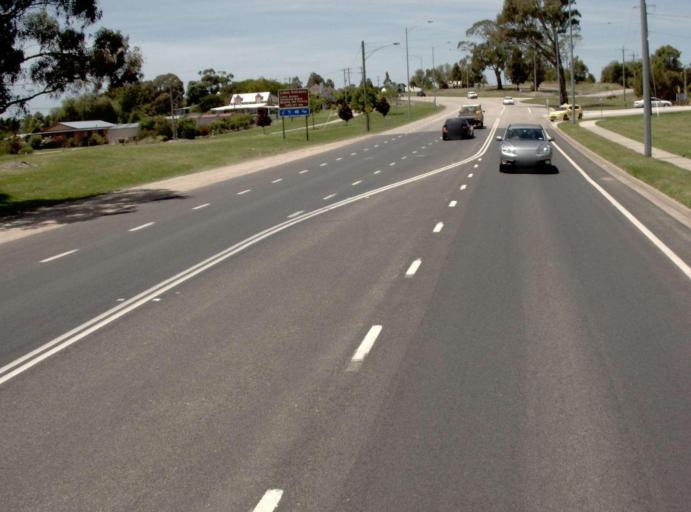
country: AU
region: Victoria
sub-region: East Gippsland
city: Bairnsdale
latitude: -37.8239
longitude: 147.6439
